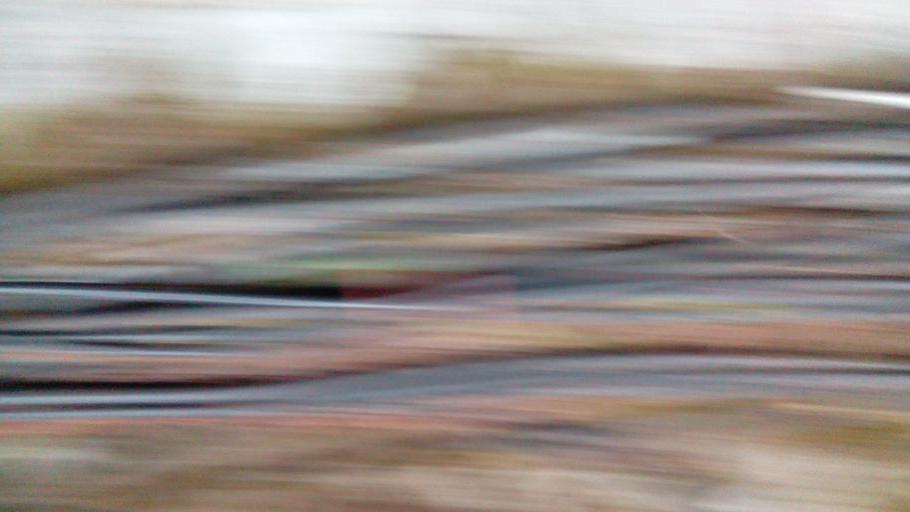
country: TW
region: Taiwan
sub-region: Nantou
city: Puli
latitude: 24.2559
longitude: 121.2522
